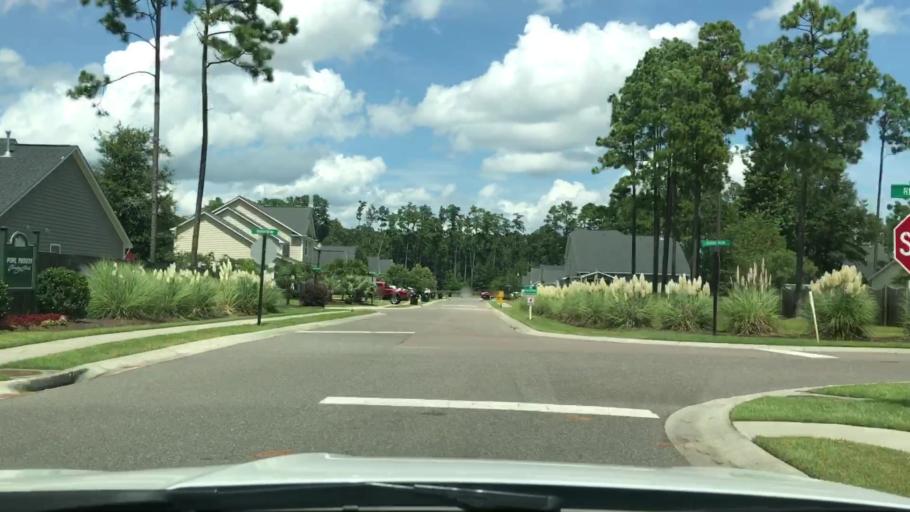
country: US
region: South Carolina
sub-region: Dorchester County
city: Summerville
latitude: 33.0374
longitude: -80.2175
